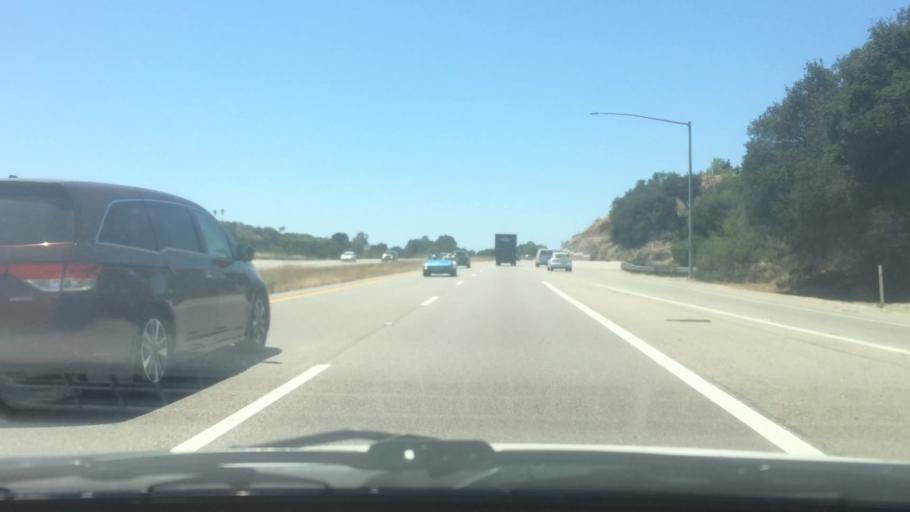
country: US
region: California
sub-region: San Luis Obispo County
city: Grover Beach
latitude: 35.1306
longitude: -120.6081
